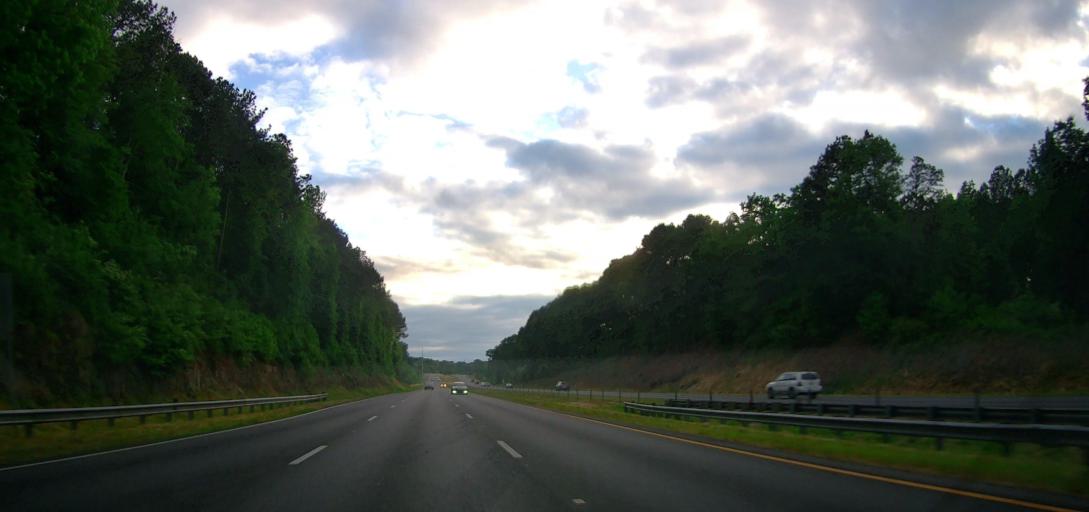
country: US
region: Georgia
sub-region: Clarke County
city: Athens
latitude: 33.9730
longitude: -83.3952
